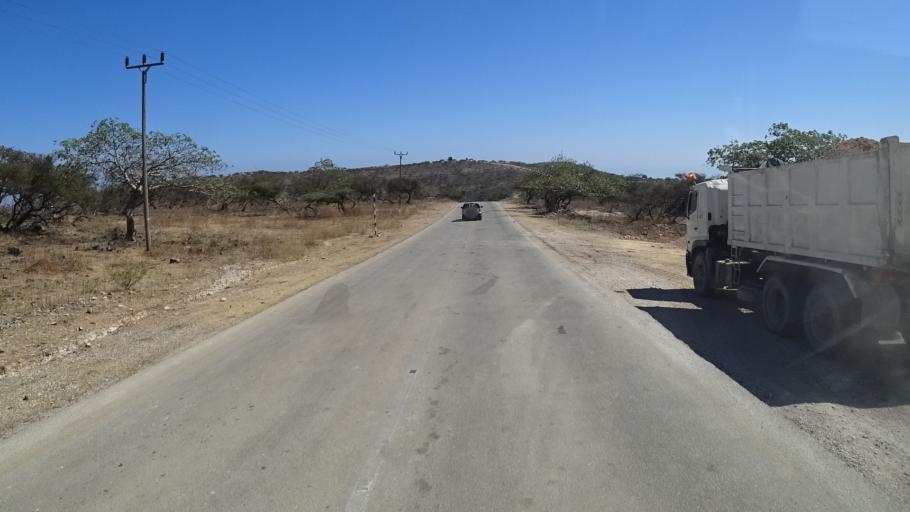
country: YE
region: Al Mahrah
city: Hawf
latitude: 16.7893
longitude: 53.3274
